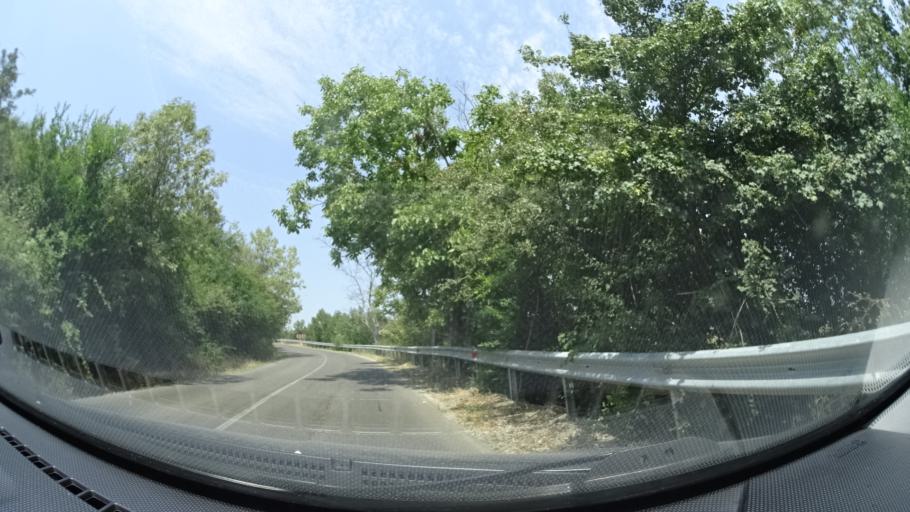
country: GE
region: Kakheti
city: Sighnaghi
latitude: 41.6223
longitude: 45.9369
